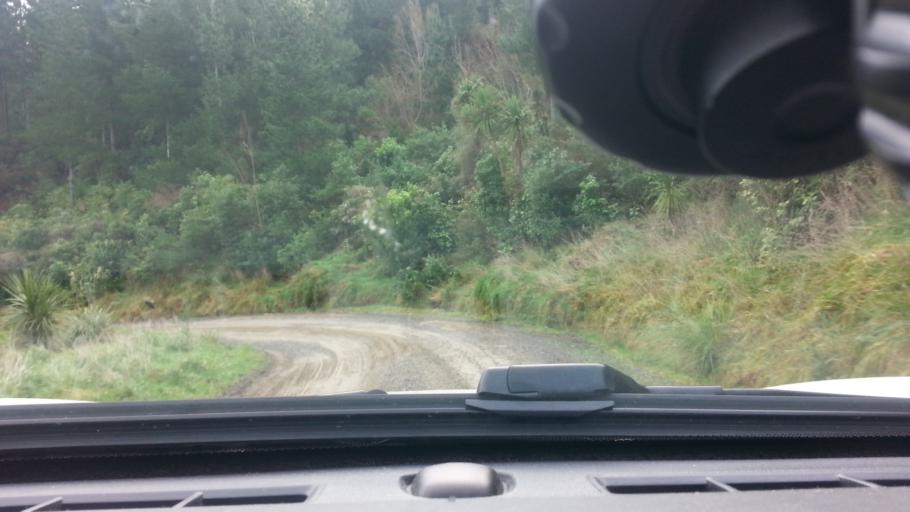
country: NZ
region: Wellington
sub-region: Masterton District
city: Masterton
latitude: -41.1853
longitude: 175.9612
